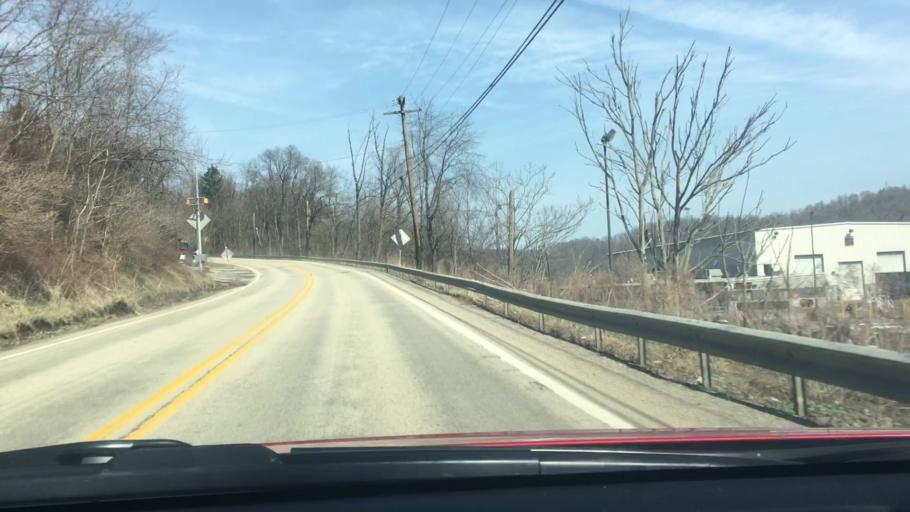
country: US
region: Pennsylvania
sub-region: Washington County
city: New Eagle
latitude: 40.2464
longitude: -79.9353
